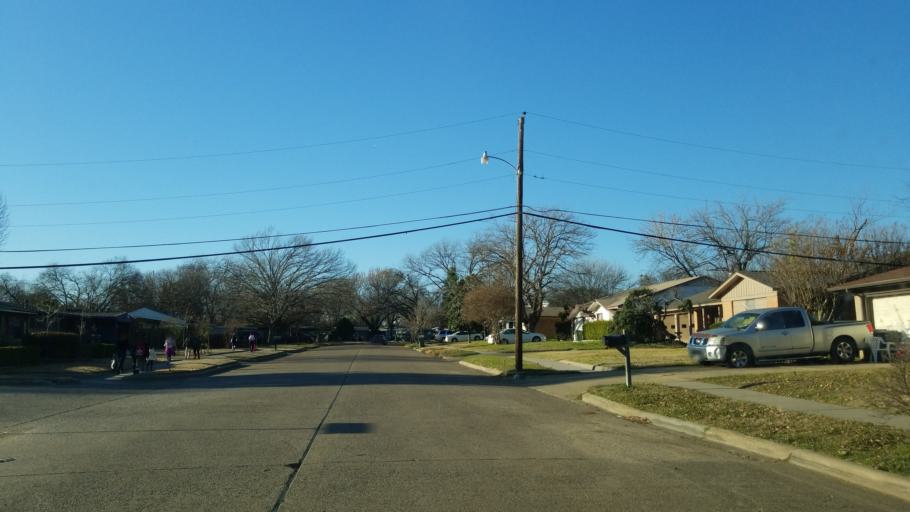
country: US
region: Texas
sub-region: Tarrant County
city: Arlington
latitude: 32.7321
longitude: -97.0680
